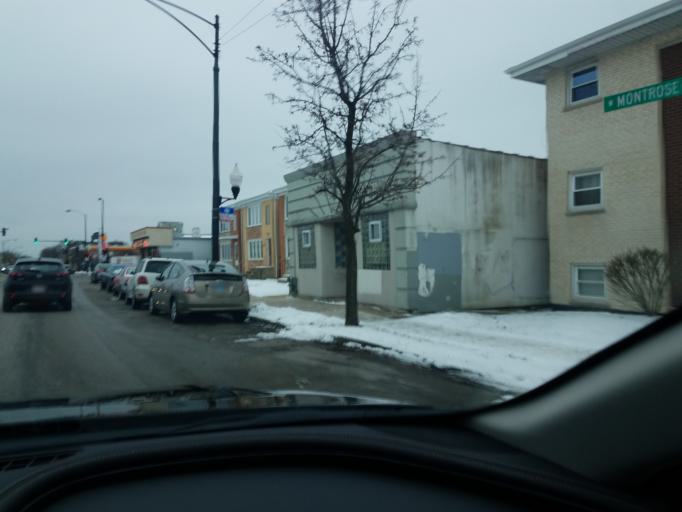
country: US
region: Illinois
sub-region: Cook County
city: Harwood Heights
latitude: 41.9603
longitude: -87.7781
